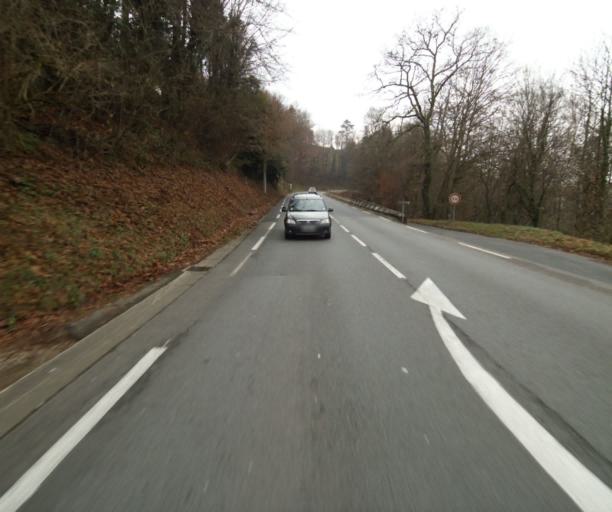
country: FR
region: Limousin
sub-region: Departement de la Correze
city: Tulle
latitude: 45.2672
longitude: 1.7424
